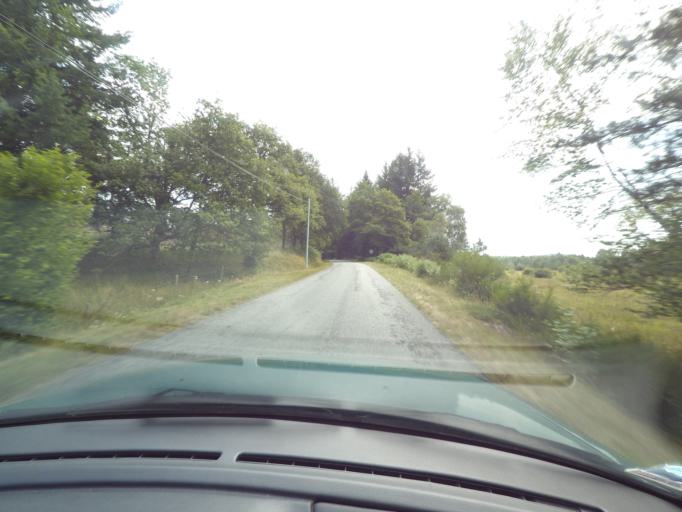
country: FR
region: Limousin
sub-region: Departement de la Correze
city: Bugeat
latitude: 45.7364
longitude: 1.9780
